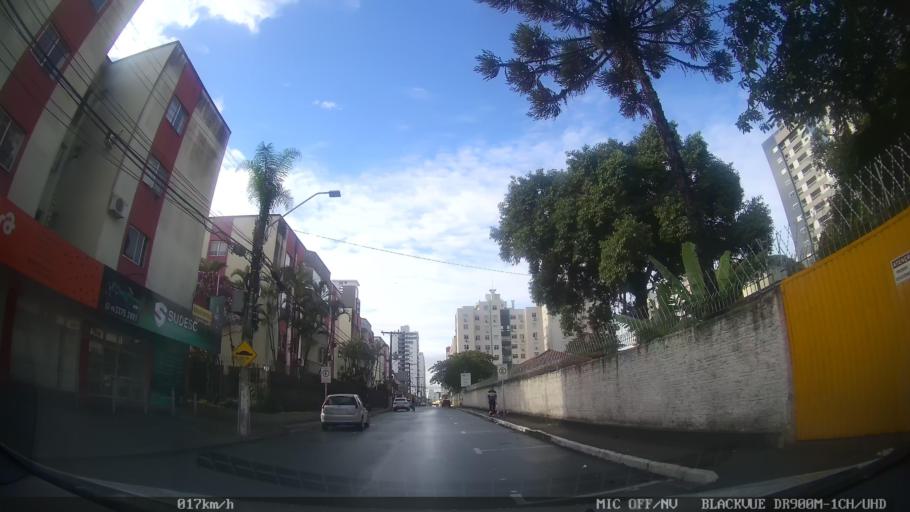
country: BR
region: Santa Catarina
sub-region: Sao Jose
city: Campinas
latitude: -27.5929
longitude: -48.6114
